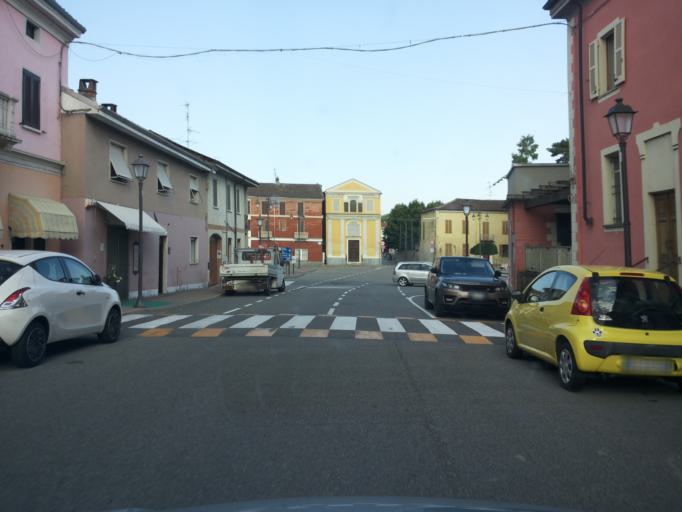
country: IT
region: Piedmont
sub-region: Provincia di Vercelli
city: Asigliano Vercellese
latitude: 45.2610
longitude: 8.4066
